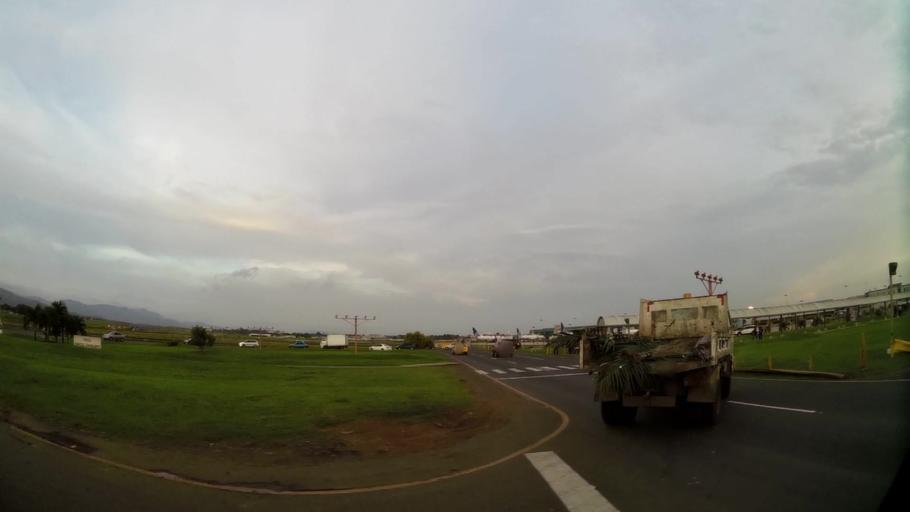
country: PA
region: Panama
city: Tocumen
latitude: 9.0709
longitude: -79.3887
